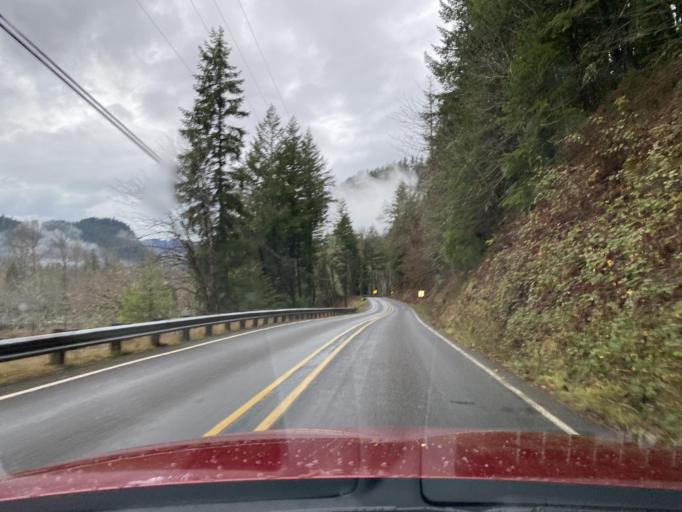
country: US
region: Oregon
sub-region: Lane County
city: Oakridge
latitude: 43.7554
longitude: -122.5258
